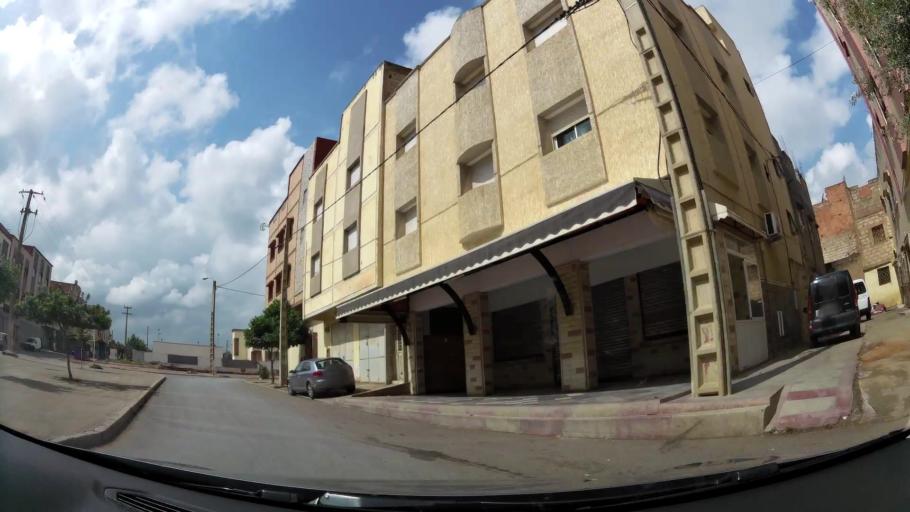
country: MA
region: Rabat-Sale-Zemmour-Zaer
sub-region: Khemisset
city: Tiflet
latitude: 33.8965
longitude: -6.3270
